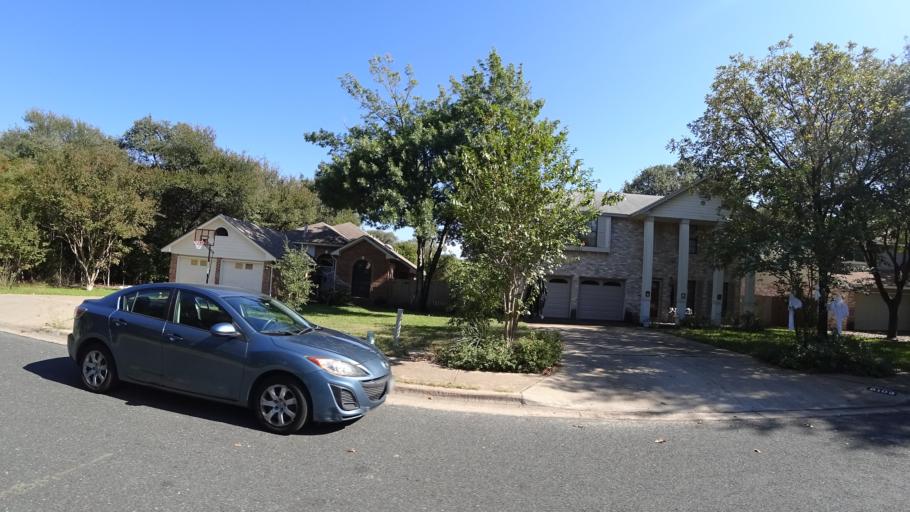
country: US
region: Texas
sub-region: Travis County
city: Shady Hollow
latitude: 30.2161
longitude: -97.8676
